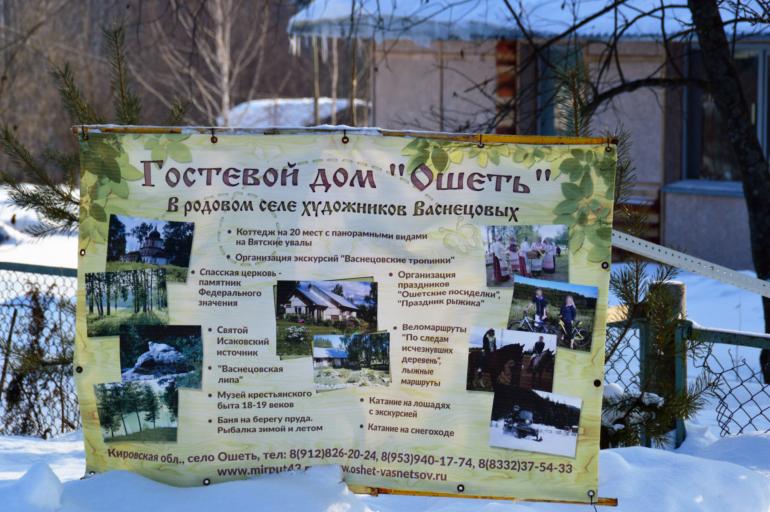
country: RU
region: Kirov
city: Kumeny
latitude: 58.0035
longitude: 50.0481
